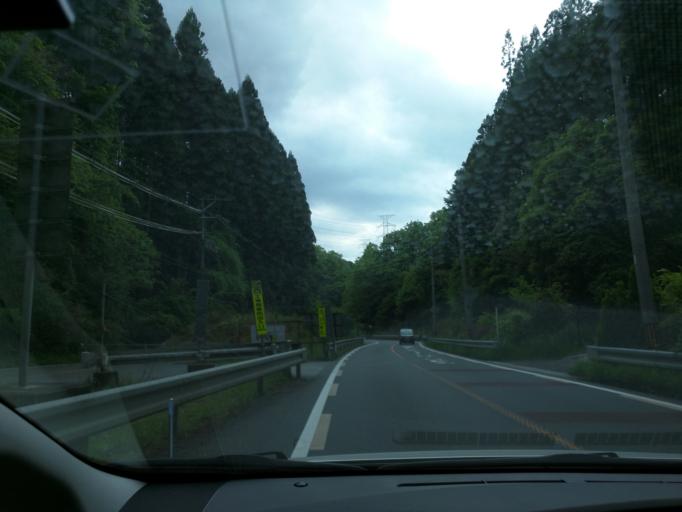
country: JP
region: Kyoto
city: Uji
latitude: 34.8576
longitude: 135.9147
